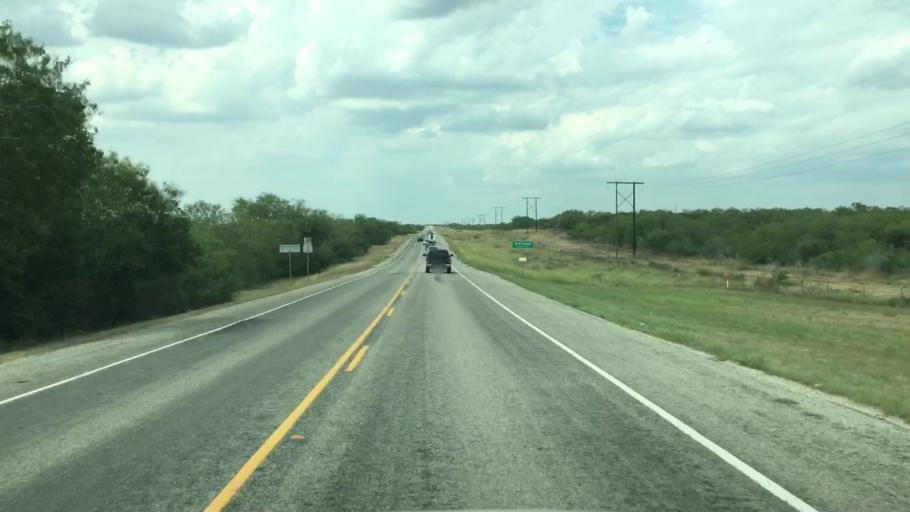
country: US
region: Texas
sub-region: Live Oak County
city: Three Rivers
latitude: 28.6489
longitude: -98.2850
